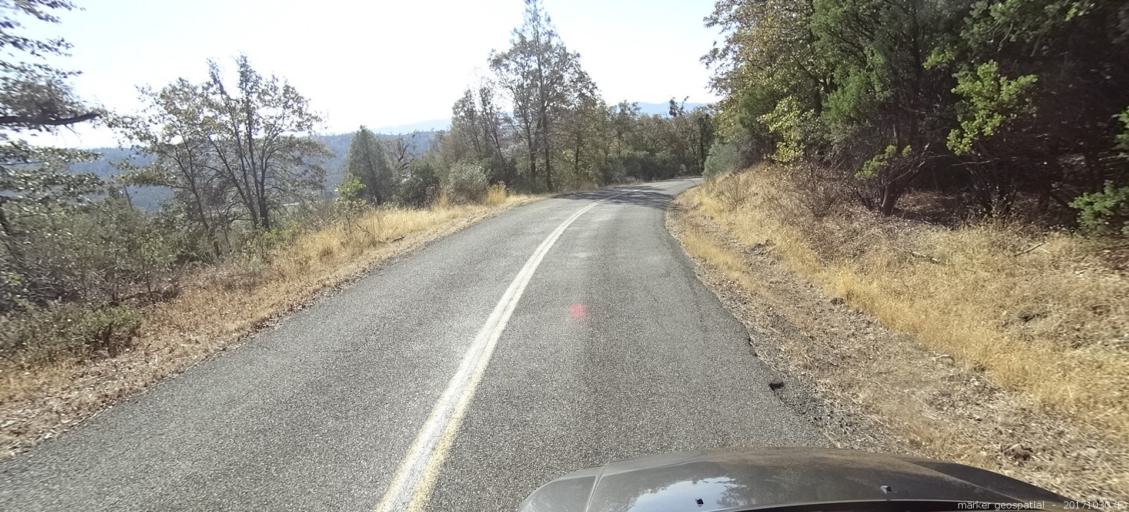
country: US
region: California
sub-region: Shasta County
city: Shingletown
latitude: 40.6416
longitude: -121.9443
